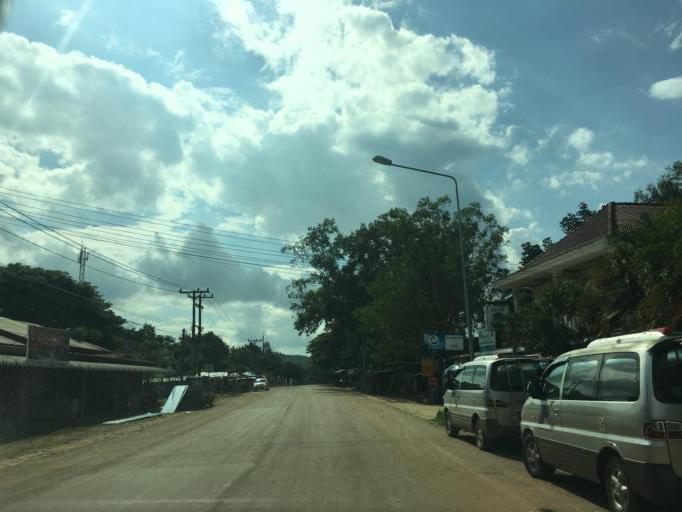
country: TH
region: Nong Khai
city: Sangkhom
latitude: 18.2180
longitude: 102.2377
